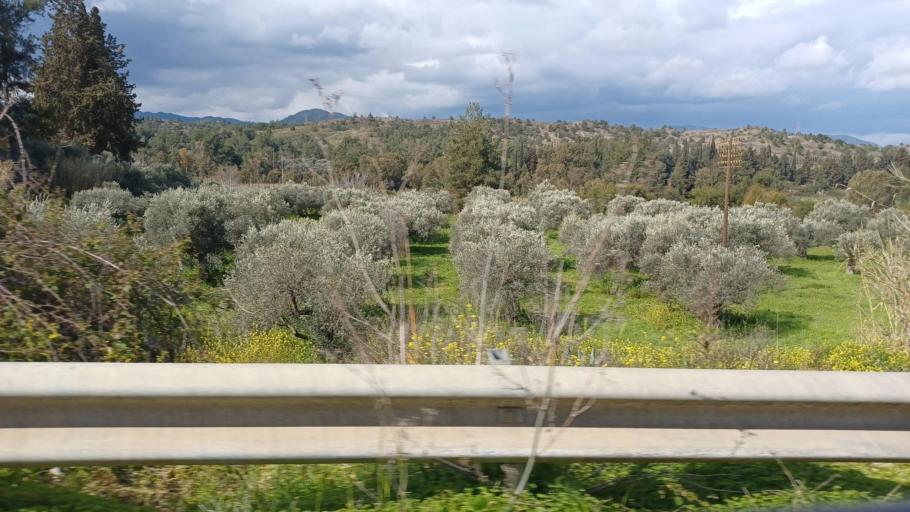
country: CY
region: Lefkosia
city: Lefka
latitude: 35.0929
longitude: 32.8846
